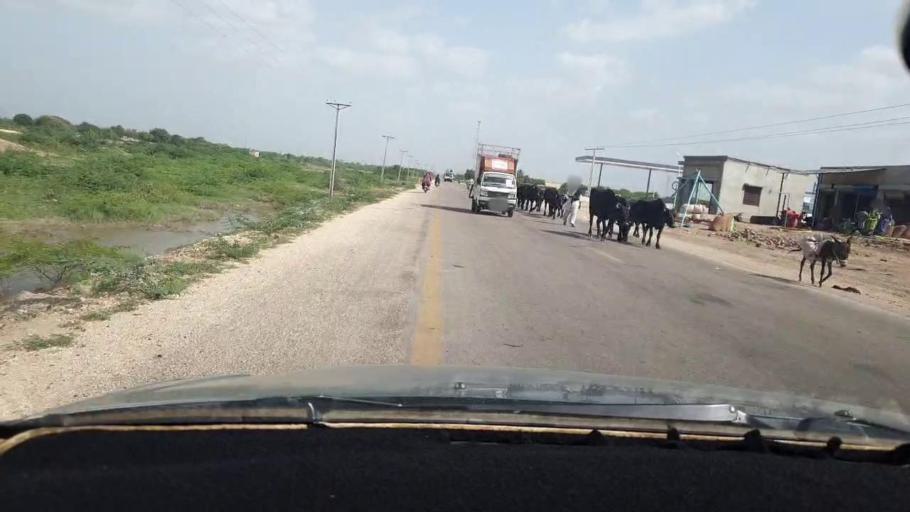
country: PK
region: Sindh
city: Naukot
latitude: 24.8678
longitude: 69.3805
